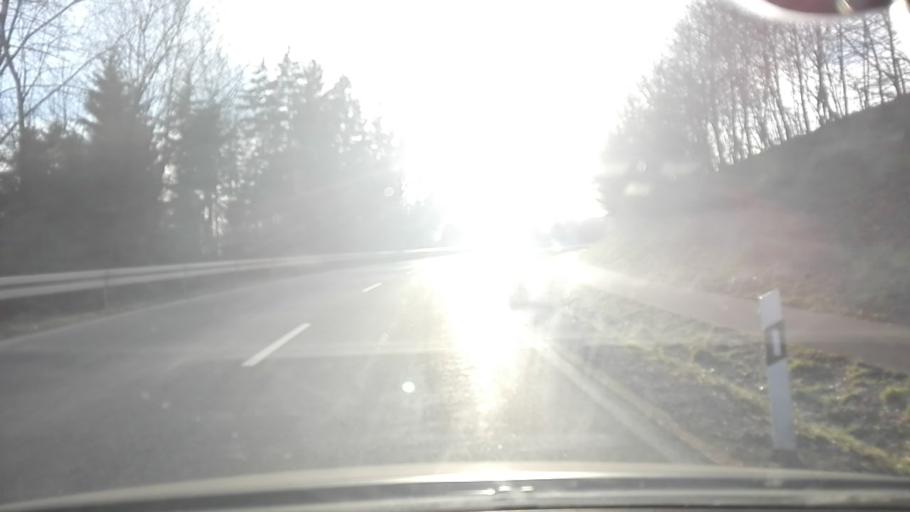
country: DE
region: North Rhine-Westphalia
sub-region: Regierungsbezirk Arnsberg
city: Schmallenberg
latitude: 51.1546
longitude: 8.2758
